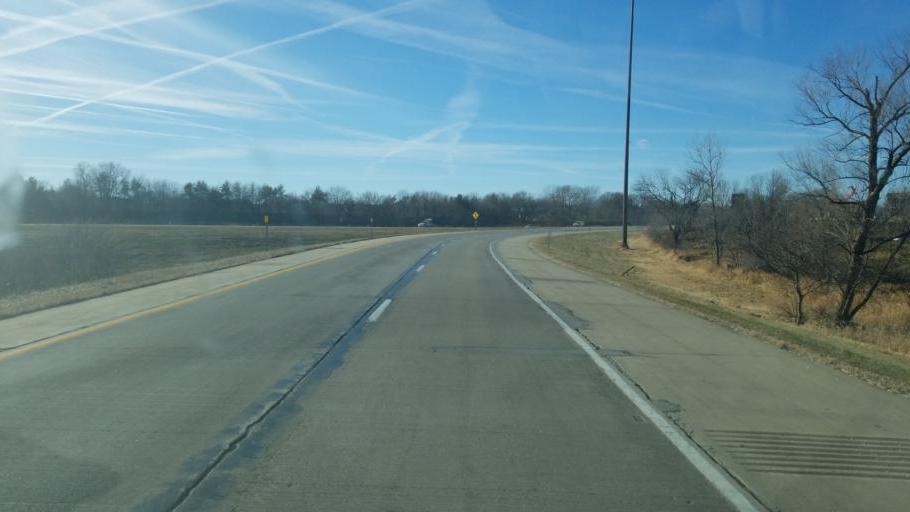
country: US
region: Iowa
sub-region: Polk County
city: Clive
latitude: 41.5932
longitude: -93.7820
